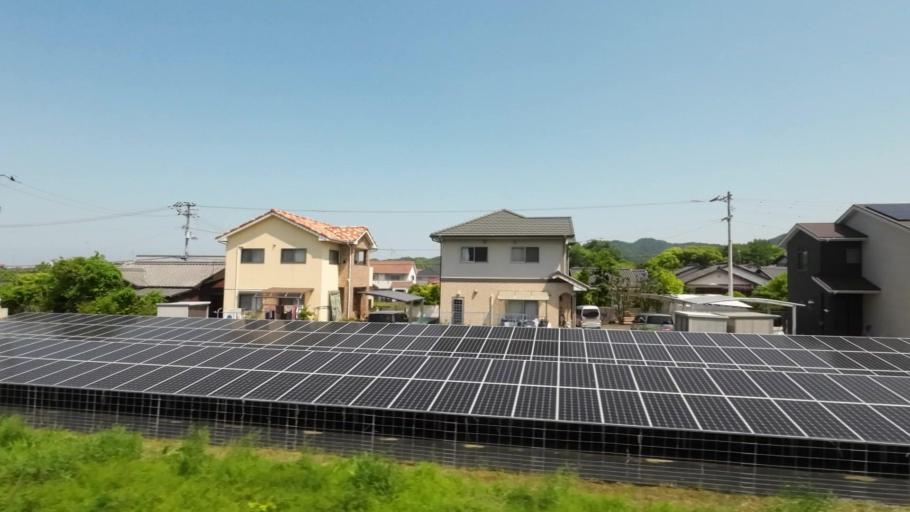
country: JP
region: Ehime
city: Saijo
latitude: 33.9217
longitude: 133.2227
